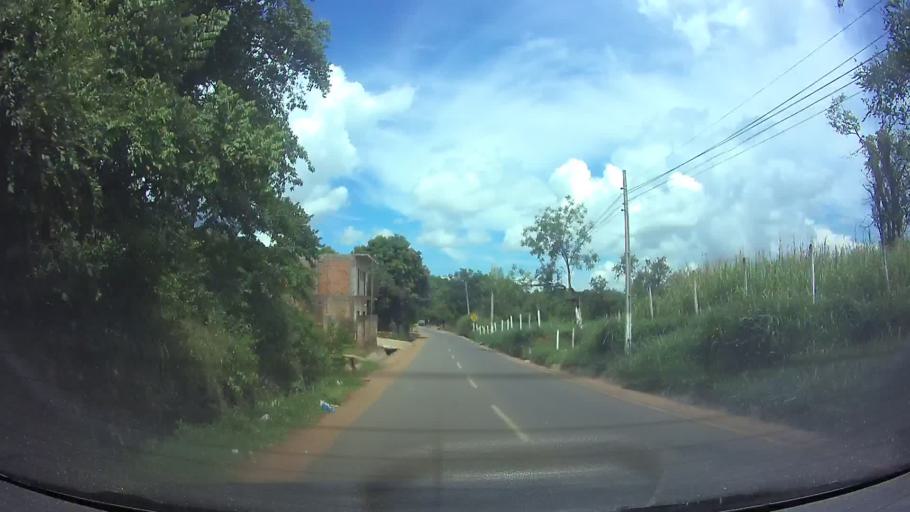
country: PY
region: Central
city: San Lorenzo
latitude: -25.3048
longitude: -57.4927
